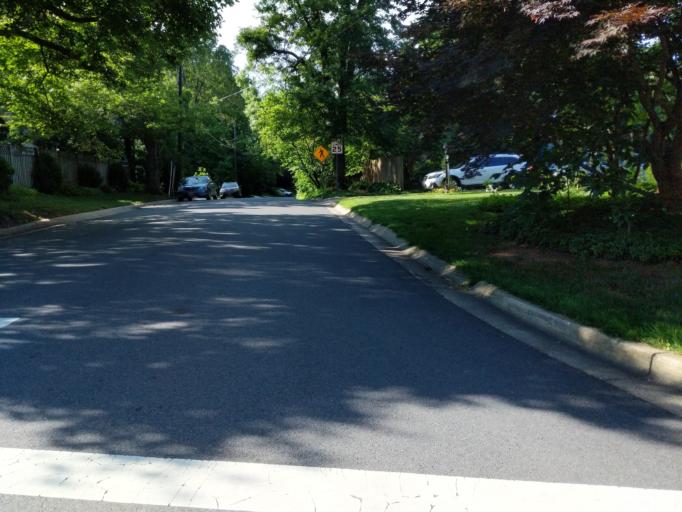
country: US
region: Maryland
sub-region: Montgomery County
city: Bethesda
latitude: 39.0051
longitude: -77.1210
